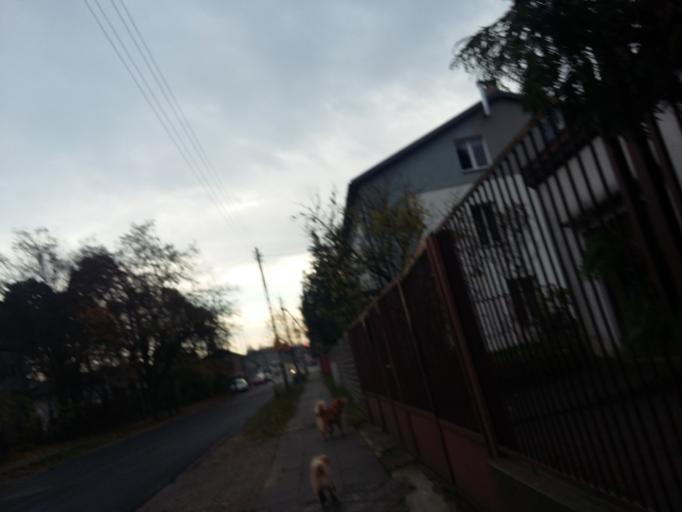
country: PL
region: Lodz Voivodeship
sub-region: Powiat pabianicki
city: Ksawerow
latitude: 51.7123
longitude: 19.4259
